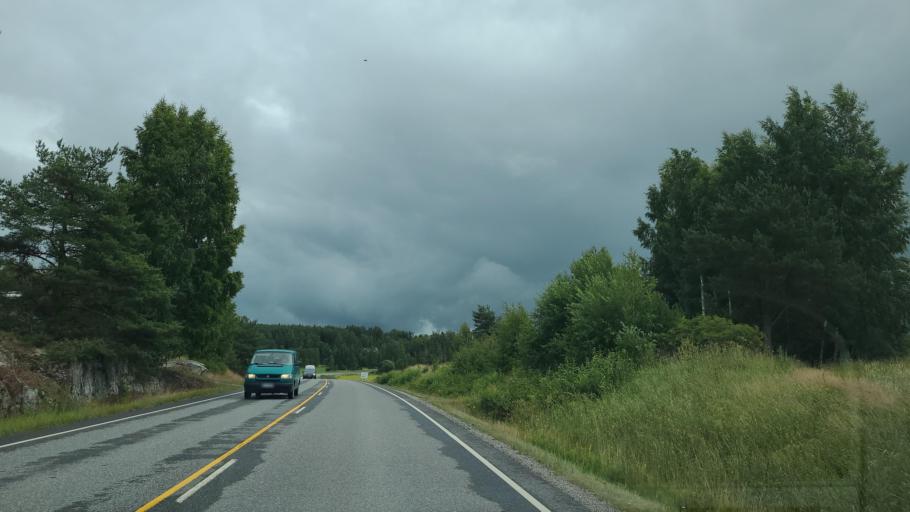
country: FI
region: Varsinais-Suomi
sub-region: Turku
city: Sauvo
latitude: 60.3410
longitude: 22.6913
